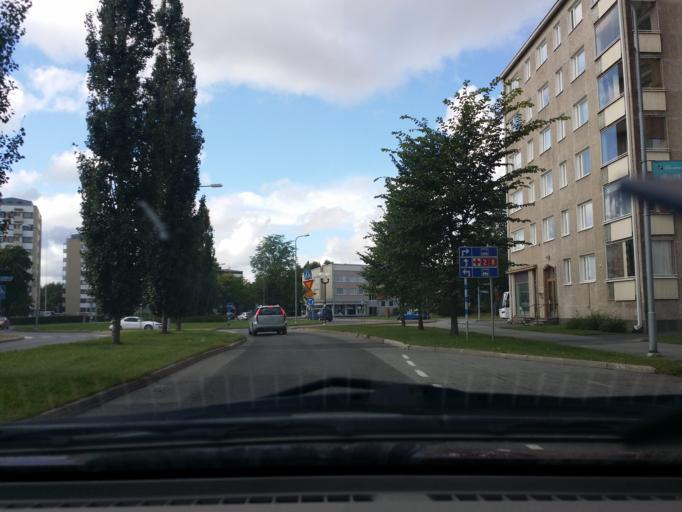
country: FI
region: Satakunta
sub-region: Pori
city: Pori
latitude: 61.4780
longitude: 21.7911
